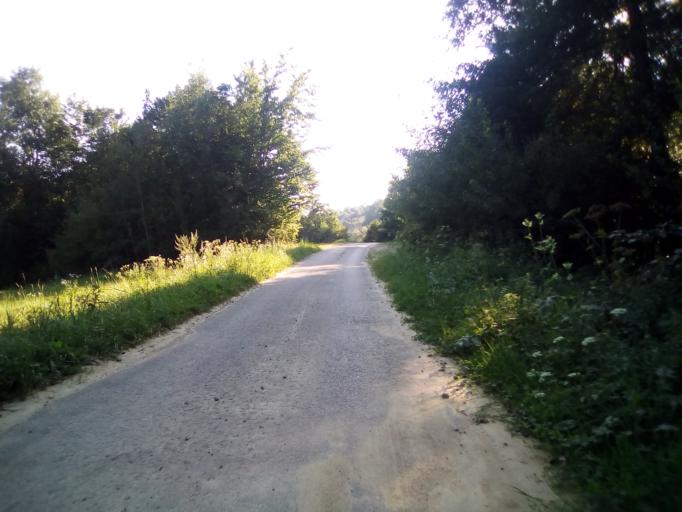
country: PL
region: Subcarpathian Voivodeship
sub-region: Powiat brzozowski
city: Domaradz
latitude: 49.8151
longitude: 21.9489
